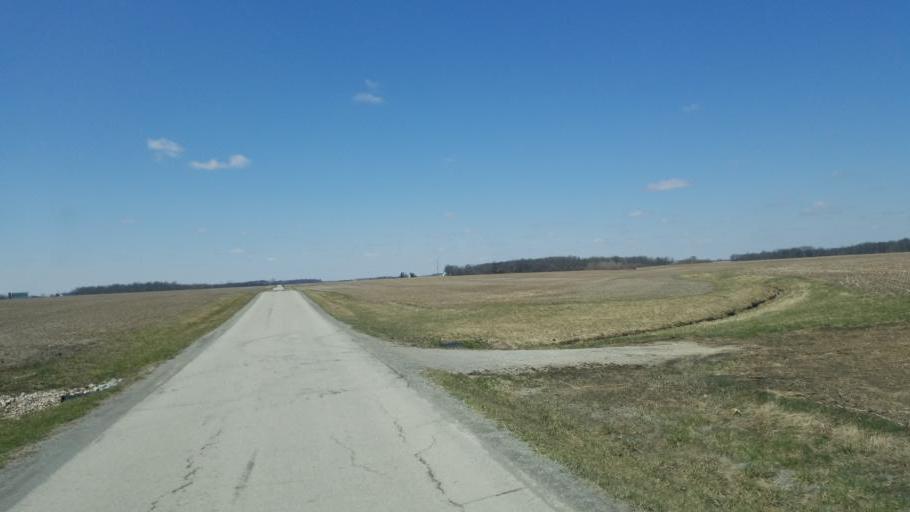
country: US
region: Ohio
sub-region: Wyandot County
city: Upper Sandusky
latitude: 40.7747
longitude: -83.2503
